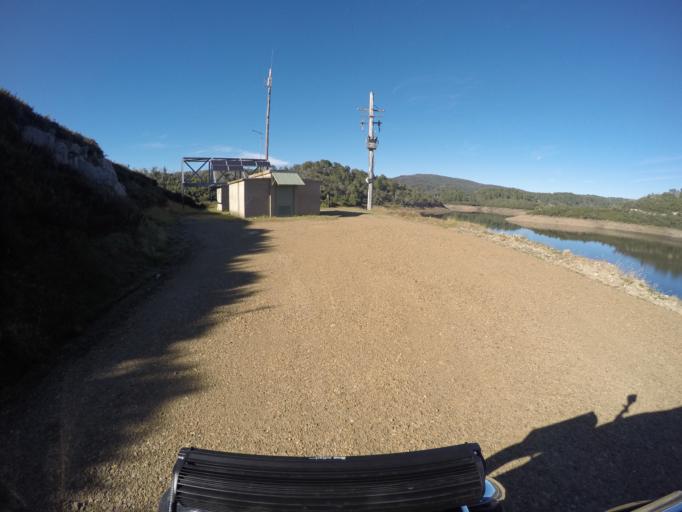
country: AU
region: New South Wales
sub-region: Snowy River
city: Jindabyne
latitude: -36.0544
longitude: 148.2783
